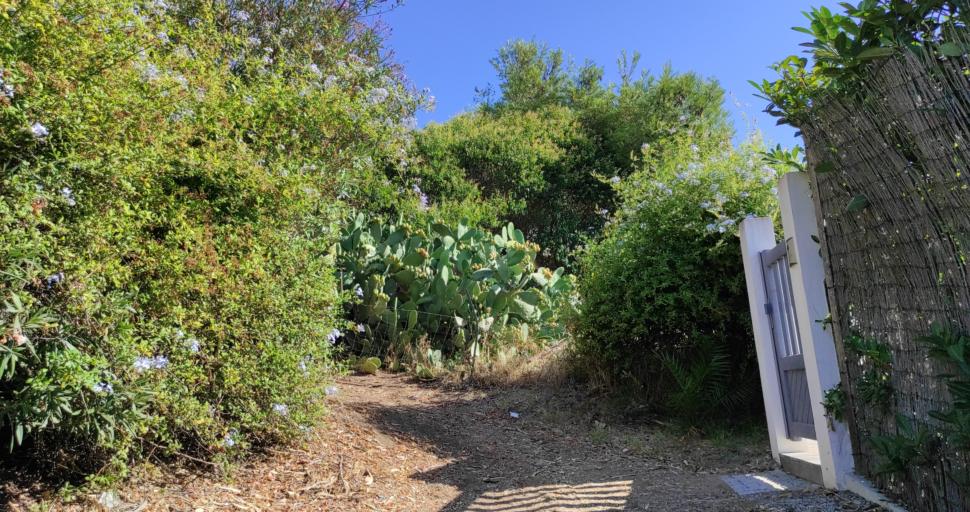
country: FR
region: Corsica
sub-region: Departement de la Corse-du-Sud
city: Alata
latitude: 41.9955
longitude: 8.6706
